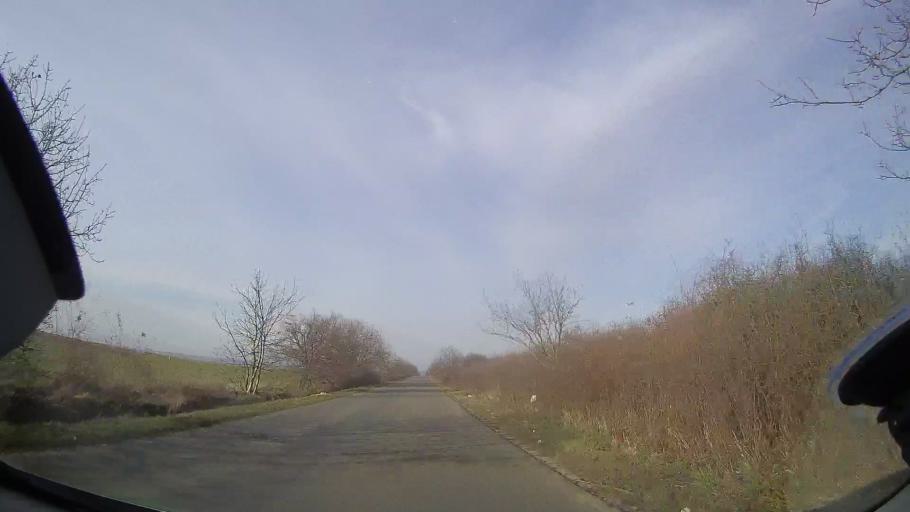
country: RO
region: Bihor
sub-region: Comuna Spinus
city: Spinus
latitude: 47.2175
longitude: 22.1742
